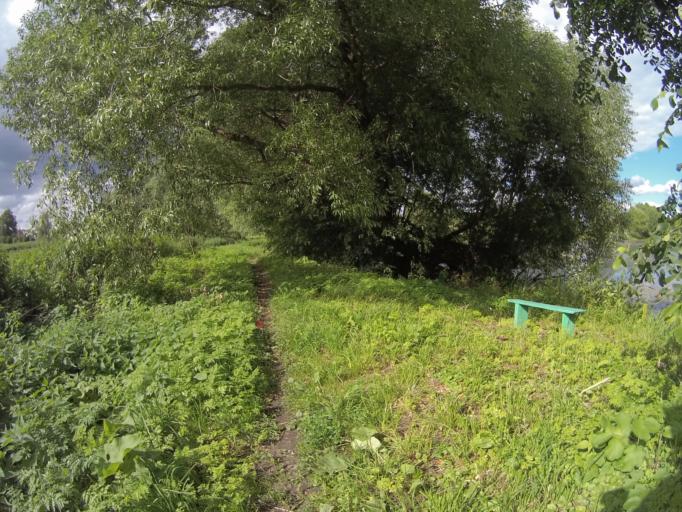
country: RU
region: Vladimir
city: Suzdal'
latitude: 56.2981
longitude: 40.3606
